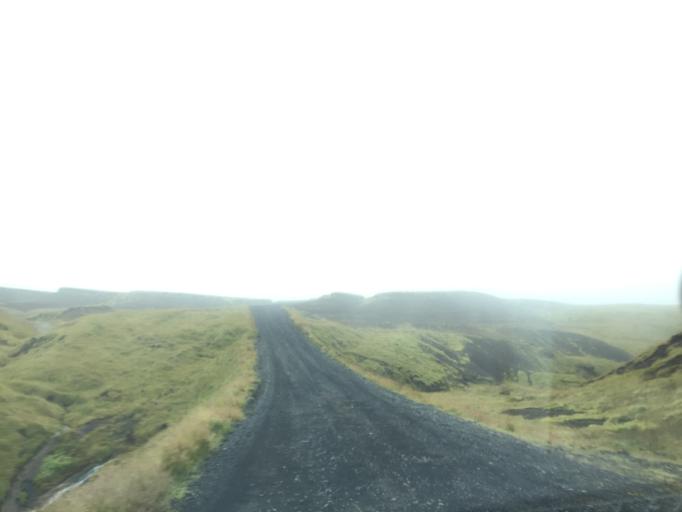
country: IS
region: South
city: Vestmannaeyjar
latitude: 63.4932
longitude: -18.8790
